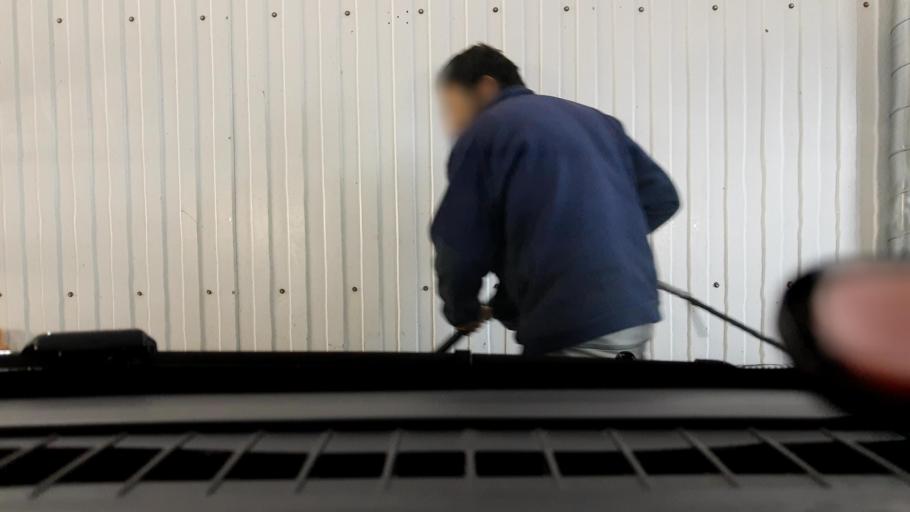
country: RU
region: Nizjnij Novgorod
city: Kstovo
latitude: 56.1390
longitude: 44.2006
